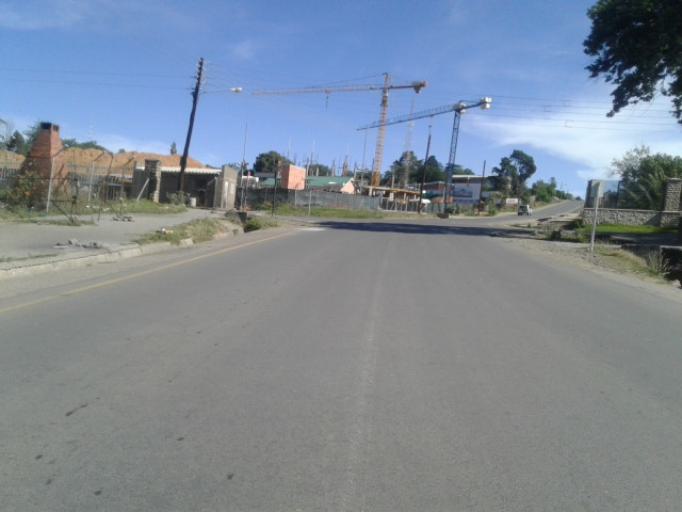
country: LS
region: Maseru
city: Maseru
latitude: -29.3094
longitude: 27.4854
